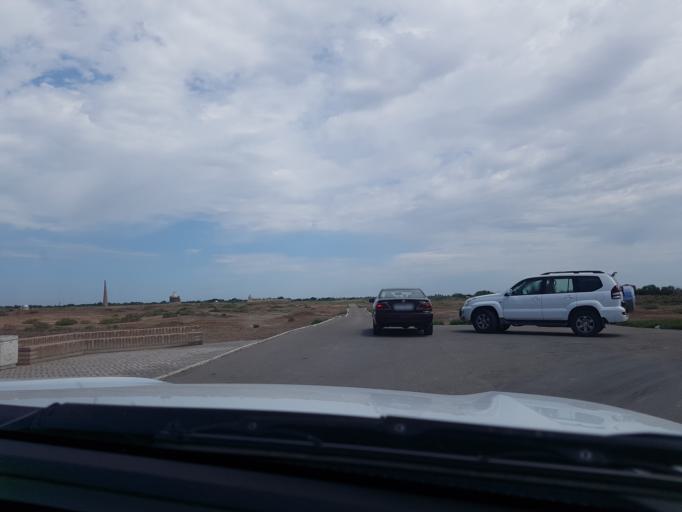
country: TM
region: Dasoguz
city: Koeneuergench
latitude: 42.2975
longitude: 59.1458
